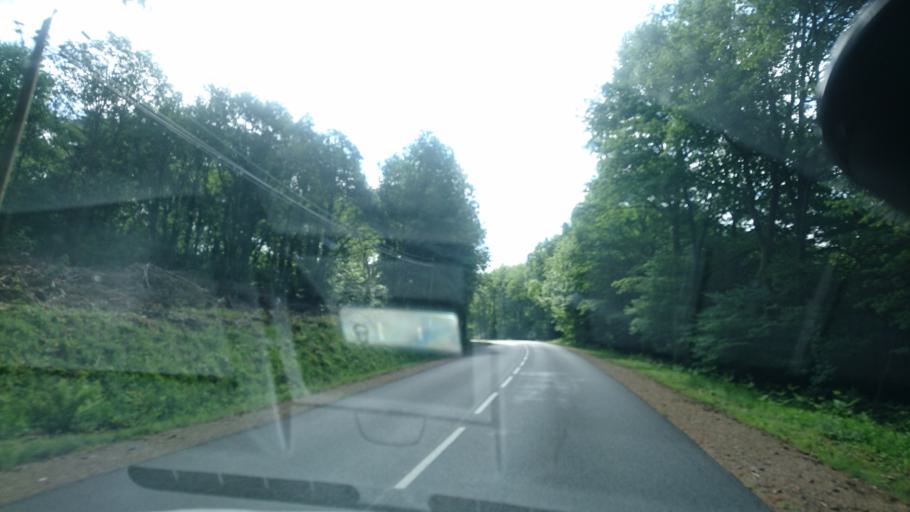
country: FR
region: Limousin
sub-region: Departement de la Haute-Vienne
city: Peyrat-le-Chateau
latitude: 45.8059
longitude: 1.8254
